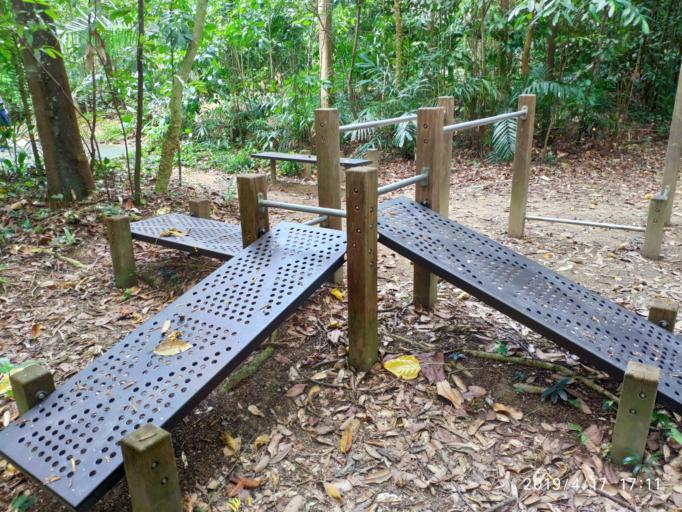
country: SG
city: Singapore
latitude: 1.3488
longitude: 103.7758
